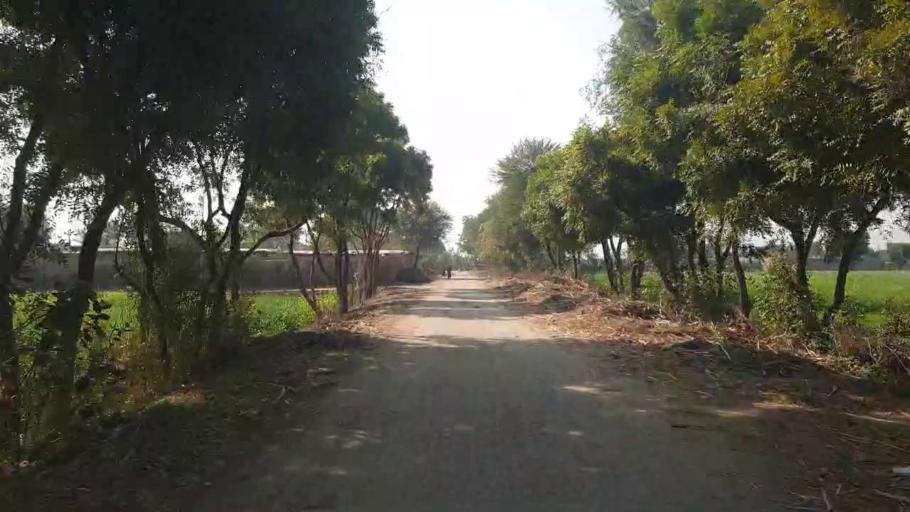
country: PK
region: Sindh
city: Tando Allahyar
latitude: 25.4596
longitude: 68.7786
